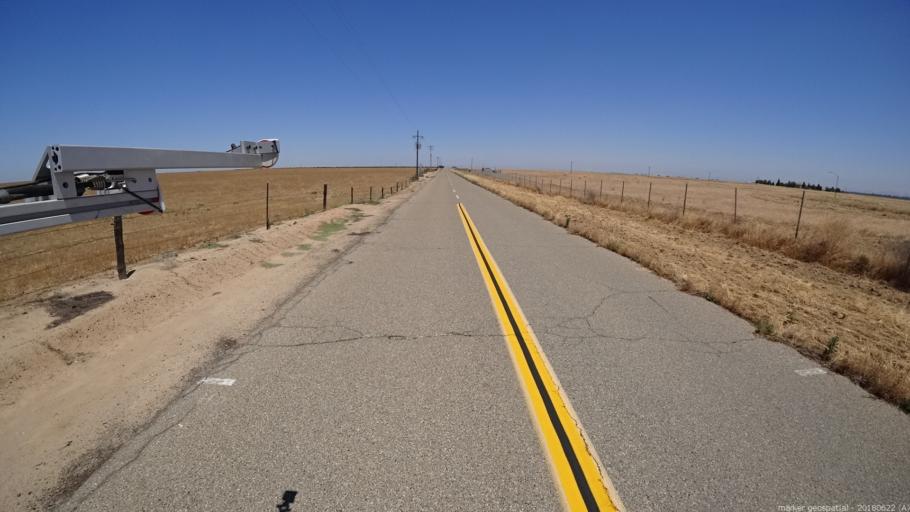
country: US
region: California
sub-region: Fresno County
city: Fresno
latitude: 36.8603
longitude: -119.8201
